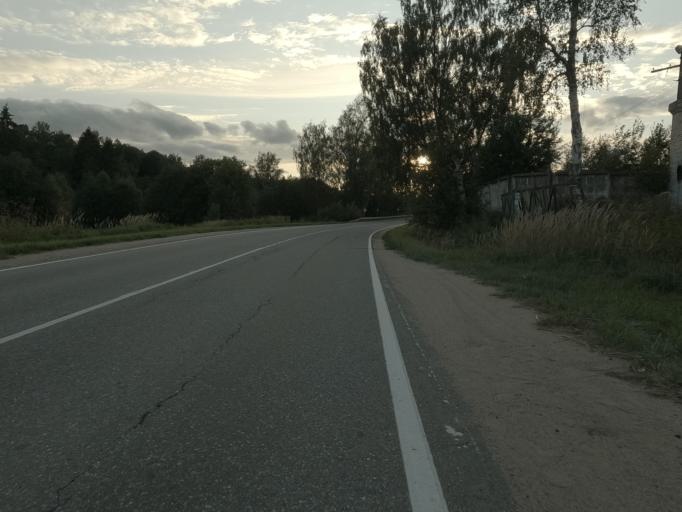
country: RU
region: Leningrad
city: Mga
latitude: 59.7545
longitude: 31.0261
